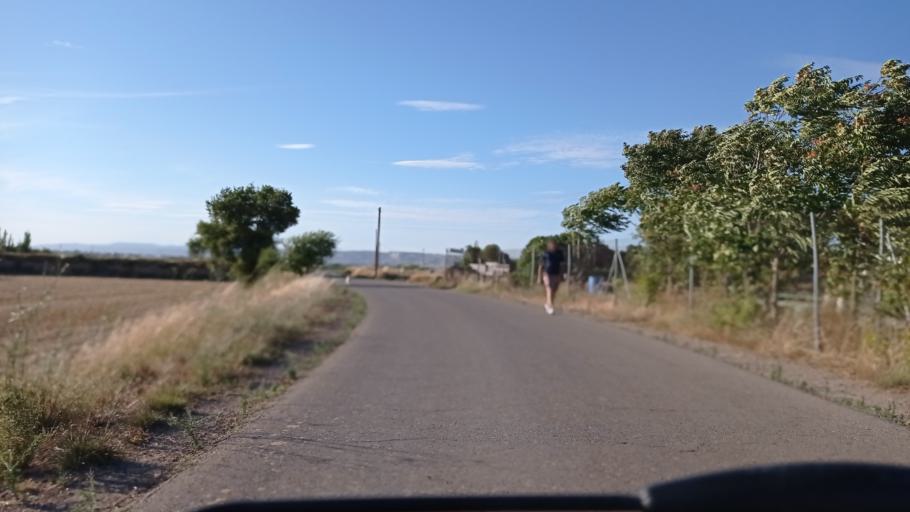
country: ES
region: Aragon
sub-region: Provincia de Zaragoza
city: Oliver-Valdefierro, Oliver, Valdefierro
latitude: 41.6682
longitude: -0.9643
